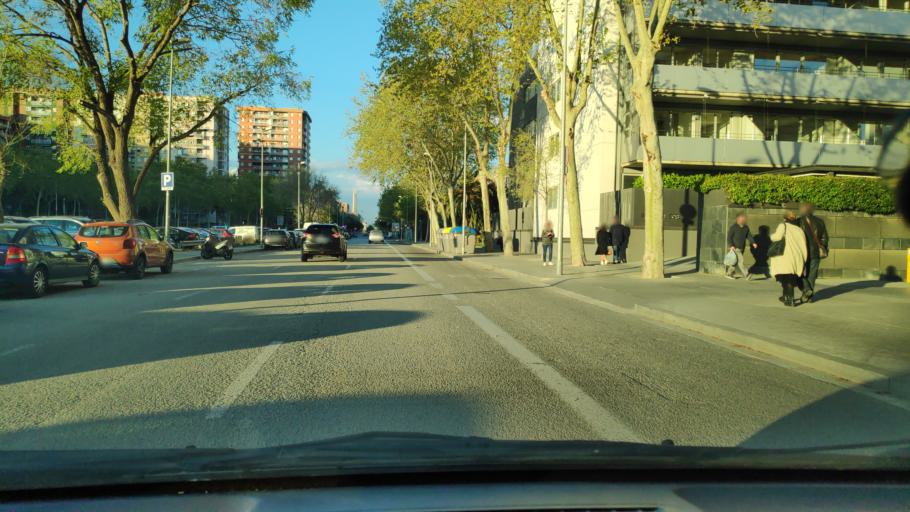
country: ES
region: Catalonia
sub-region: Provincia de Barcelona
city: Sant Marti
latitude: 41.4084
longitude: 2.2120
